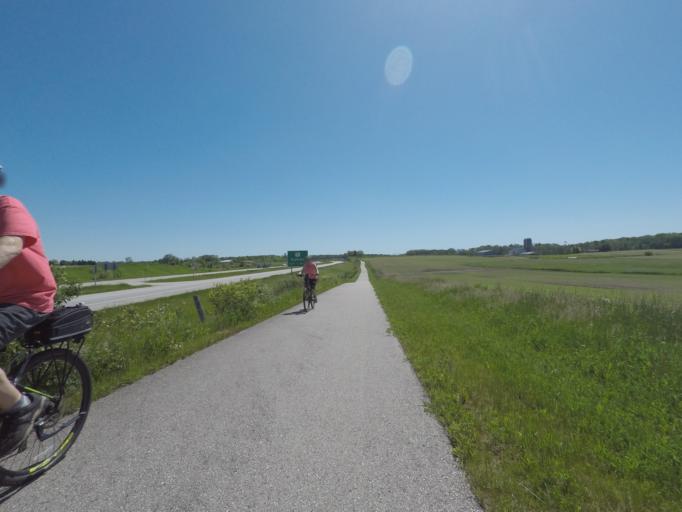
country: US
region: Wisconsin
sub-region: Sheboygan County
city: Sheboygan Falls
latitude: 43.7501
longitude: -87.8071
